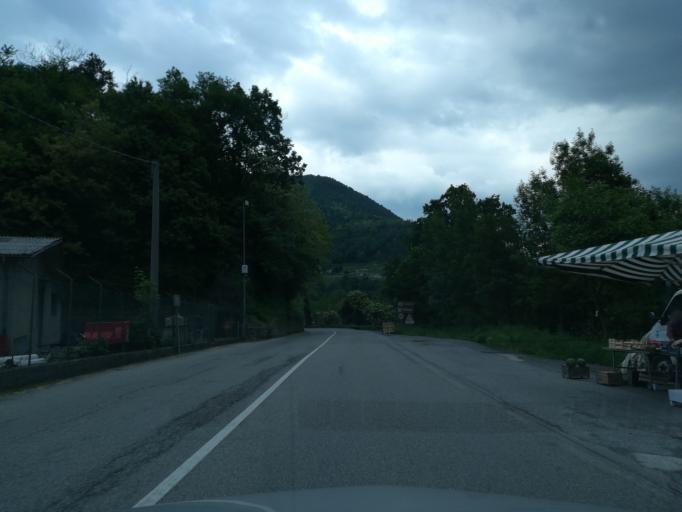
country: IT
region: Lombardy
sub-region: Provincia di Bergamo
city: Almenno San Salvatore
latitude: 45.7576
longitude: 9.5963
